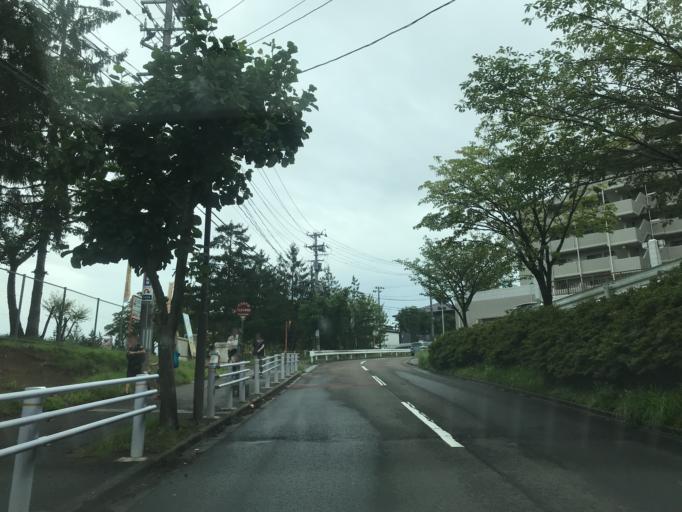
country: JP
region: Miyagi
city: Sendai-shi
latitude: 38.3072
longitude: 140.8935
